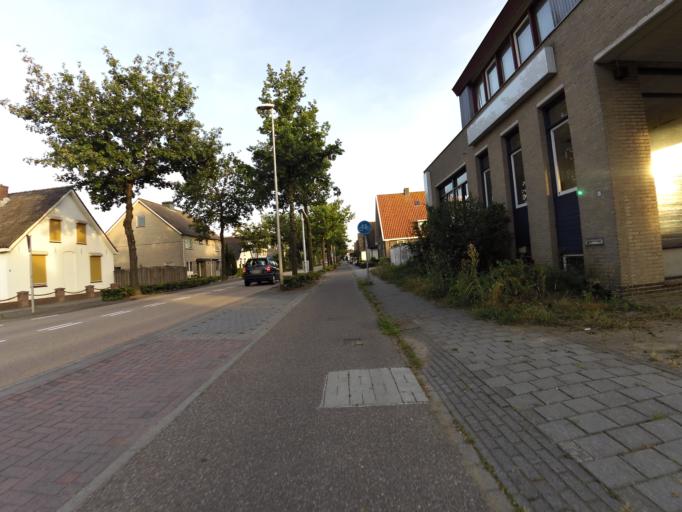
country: NL
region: Gelderland
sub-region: Gemeente Zevenaar
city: Zevenaar
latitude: 51.9078
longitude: 6.1101
